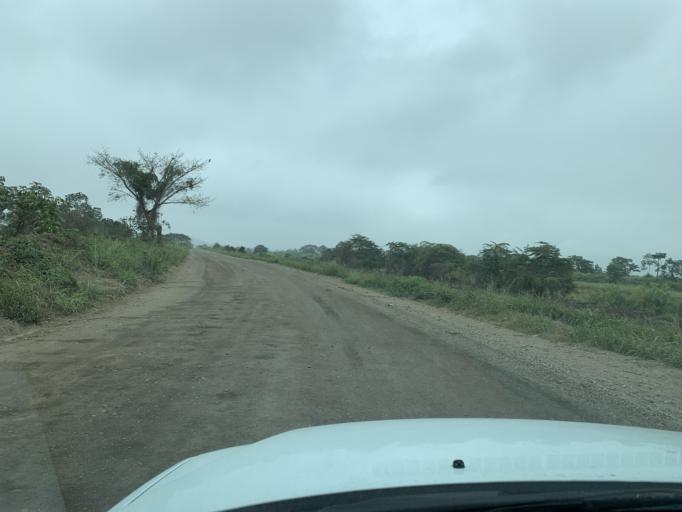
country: EC
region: Guayas
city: Coronel Marcelino Mariduena
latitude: -2.3597
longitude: -79.5817
